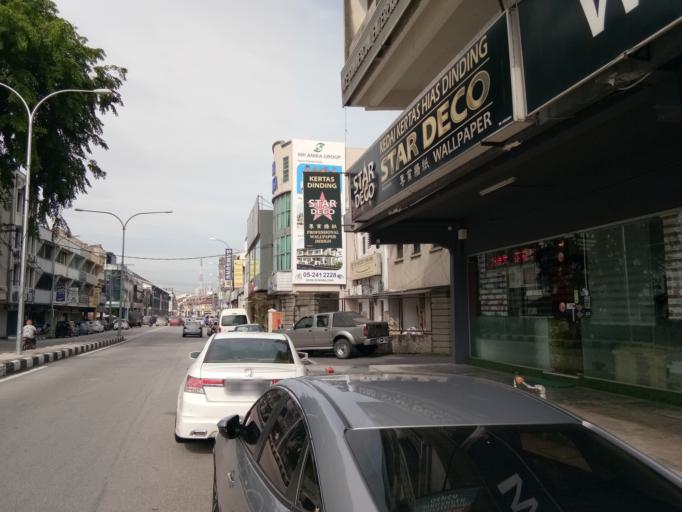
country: MY
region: Perak
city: Ipoh
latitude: 4.6006
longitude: 101.0859
